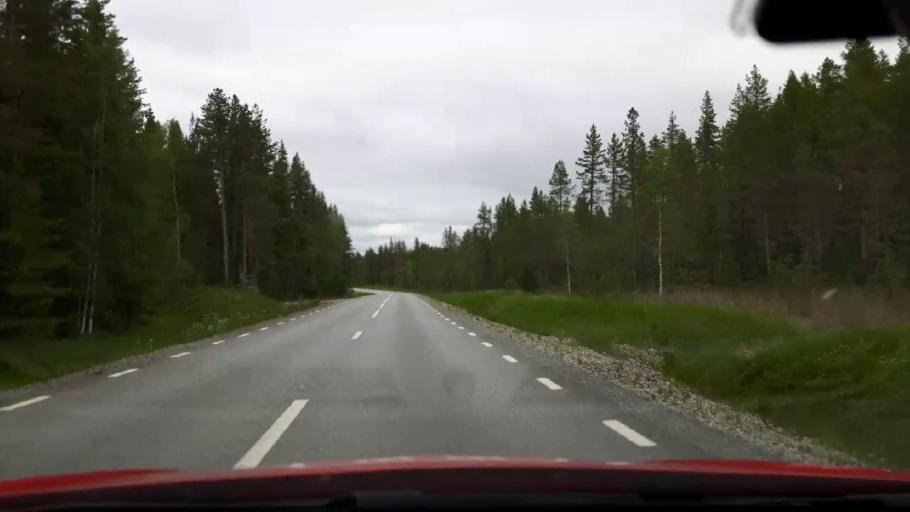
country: SE
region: Jaemtland
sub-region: OEstersunds Kommun
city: Lit
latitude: 63.6961
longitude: 14.6846
